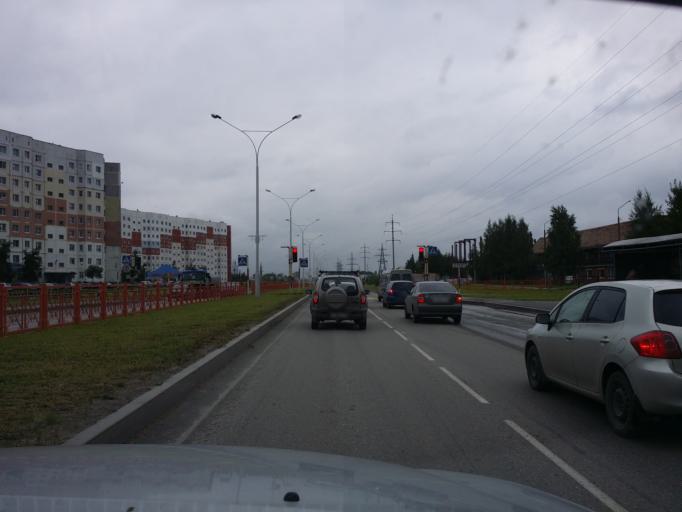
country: RU
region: Khanty-Mansiyskiy Avtonomnyy Okrug
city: Nizhnevartovsk
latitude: 60.9570
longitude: 76.5703
